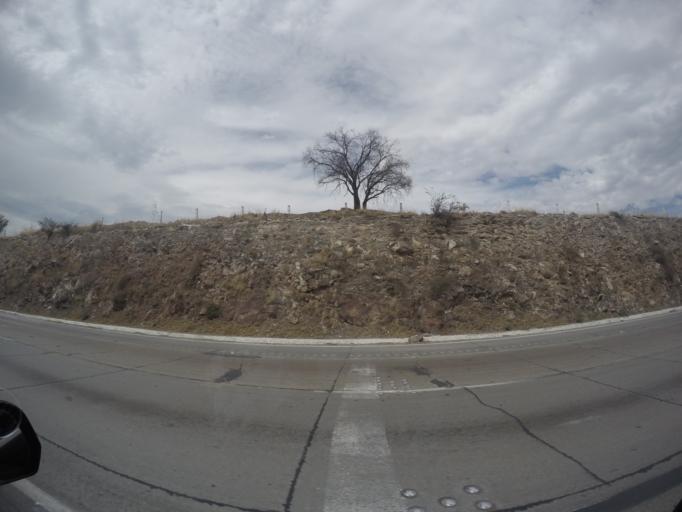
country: MX
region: Queretaro
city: San Juan del Rio
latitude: 20.3635
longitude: -99.9742
